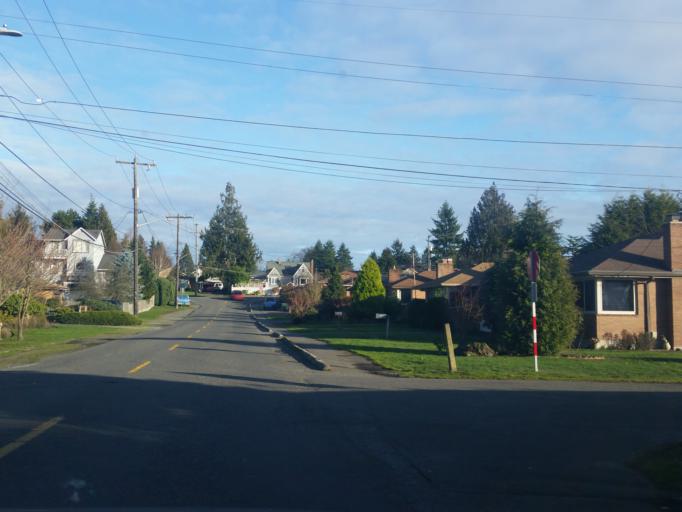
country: US
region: Washington
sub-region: King County
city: Shoreline
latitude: 47.6990
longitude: -122.3787
